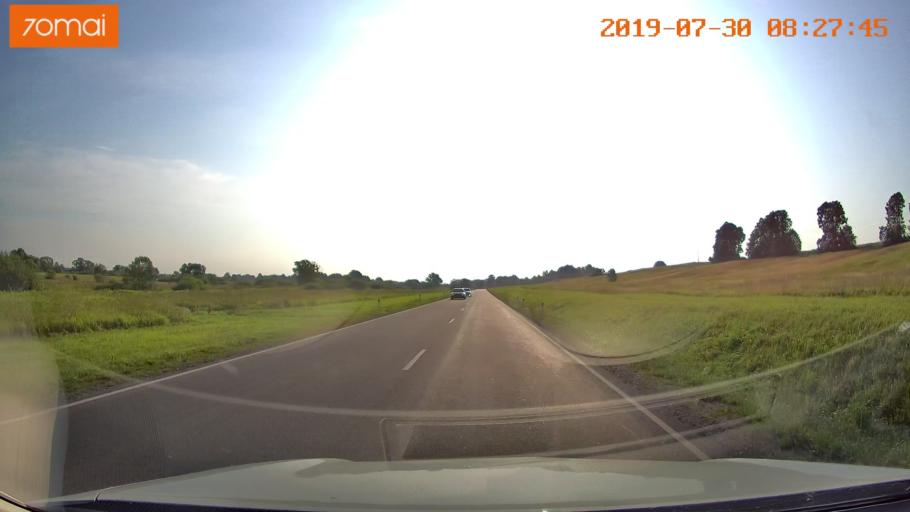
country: RU
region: Kaliningrad
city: Chernyakhovsk
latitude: 54.6282
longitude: 21.6318
